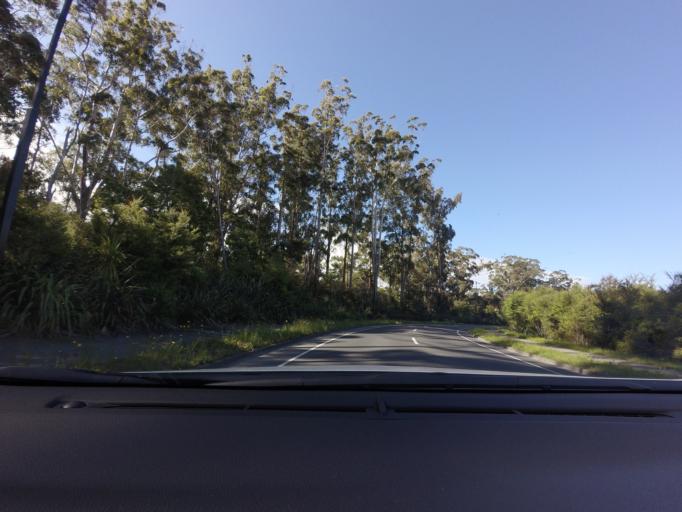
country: NZ
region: Auckland
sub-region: Auckland
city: Rothesay Bay
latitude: -36.5988
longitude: 174.6651
